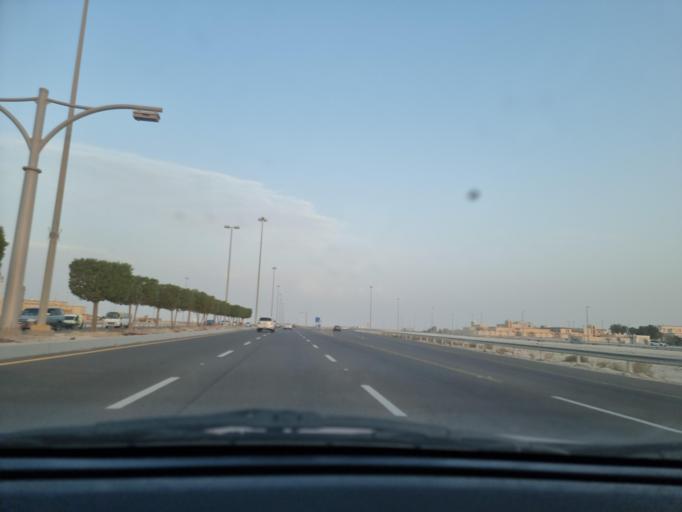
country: AE
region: Abu Dhabi
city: Abu Dhabi
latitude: 24.3820
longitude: 54.7256
